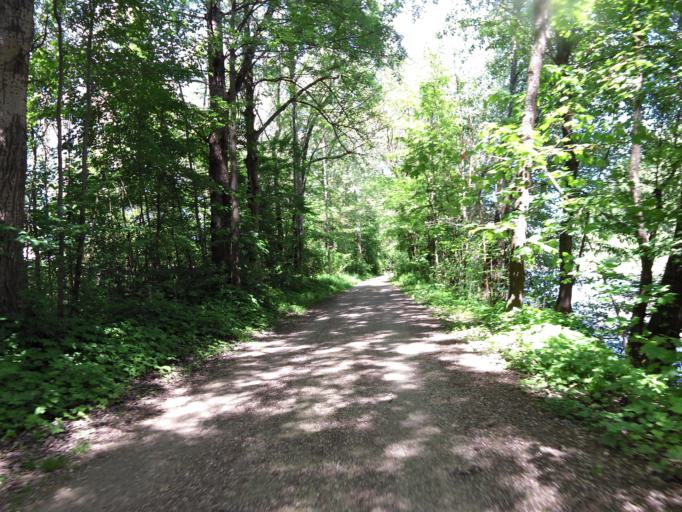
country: DE
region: Bavaria
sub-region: Upper Bavaria
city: Freising
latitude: 48.4032
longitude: 11.7616
